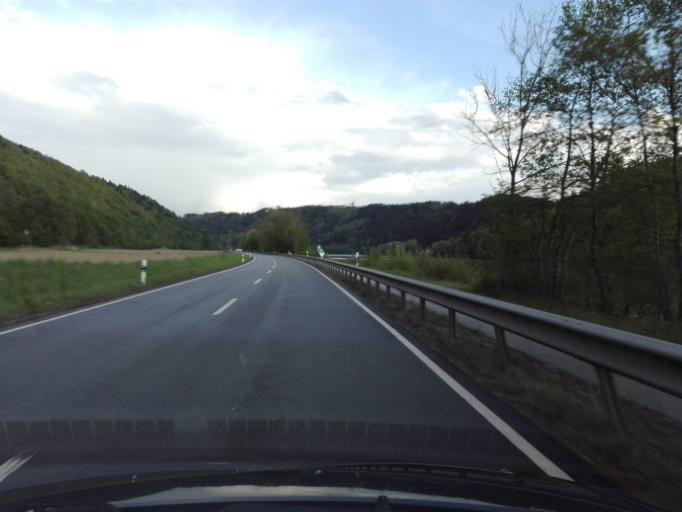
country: DE
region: Bavaria
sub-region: Lower Bavaria
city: Thyrnau
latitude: 48.5693
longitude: 13.5545
